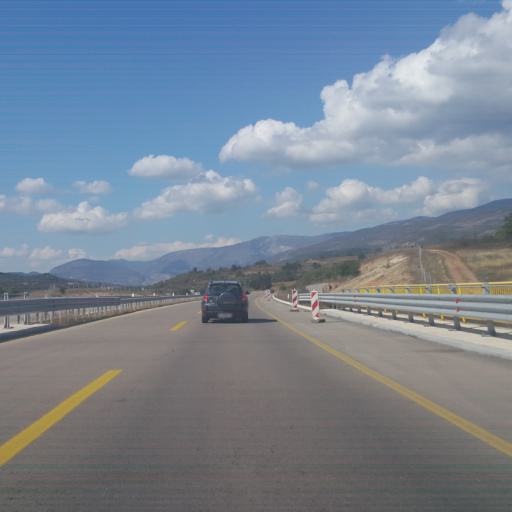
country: RS
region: Central Serbia
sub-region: Pirotski Okrug
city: Bela Palanka
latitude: 43.2426
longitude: 22.2831
